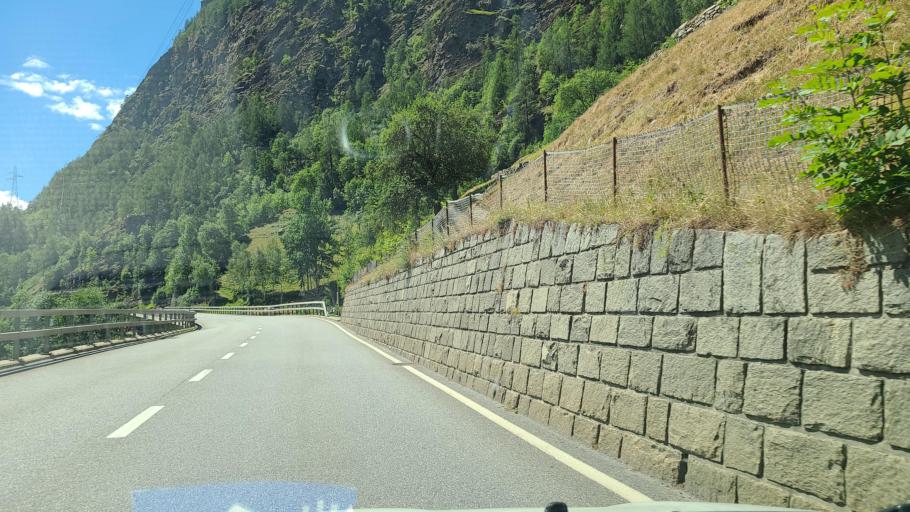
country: CH
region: Valais
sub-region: Visp District
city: Stalden
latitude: 46.2183
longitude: 7.8793
